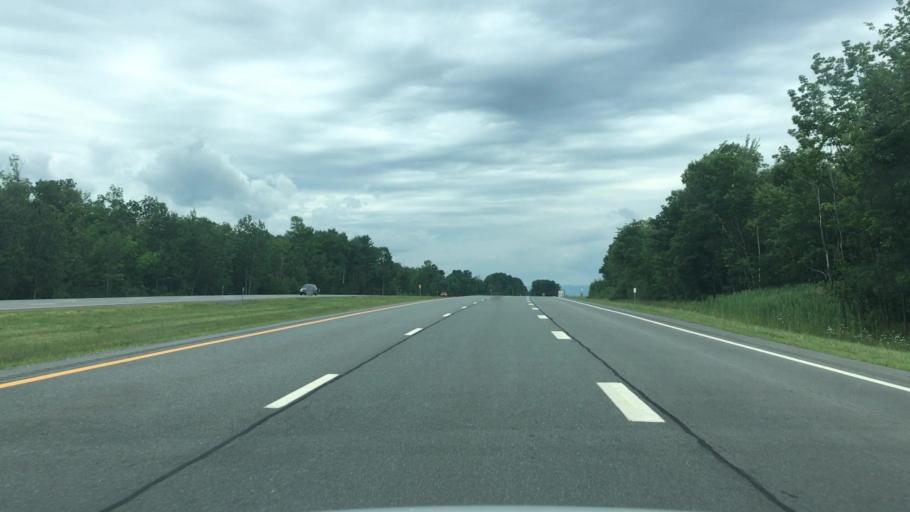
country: US
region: New York
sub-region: Schoharie County
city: Schoharie
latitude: 42.7168
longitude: -74.2604
